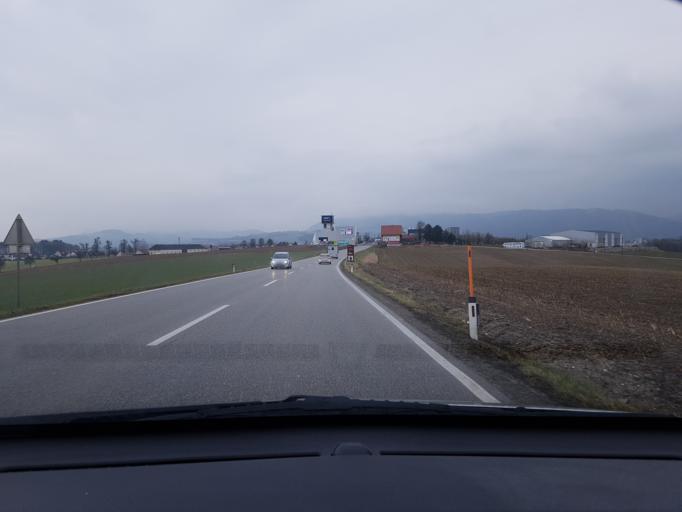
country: AT
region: Upper Austria
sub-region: Steyr Stadt
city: Steyr
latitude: 48.0545
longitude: 14.3924
